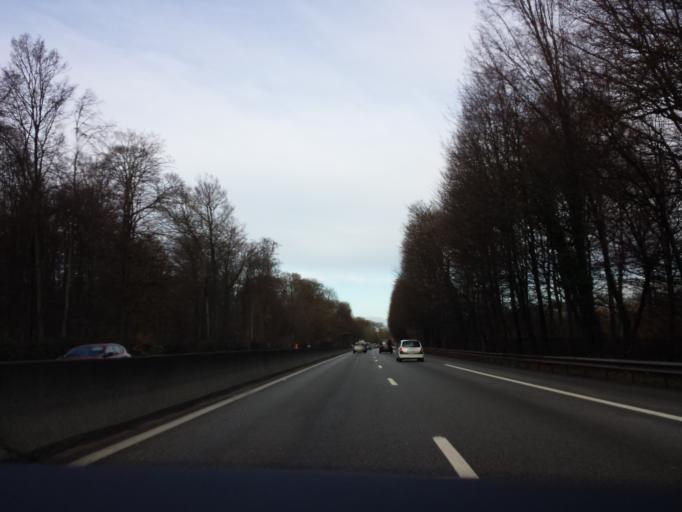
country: FR
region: Ile-de-France
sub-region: Departement des Yvelines
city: Saint-Nom-la-Breteche
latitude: 48.8817
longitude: 2.0157
